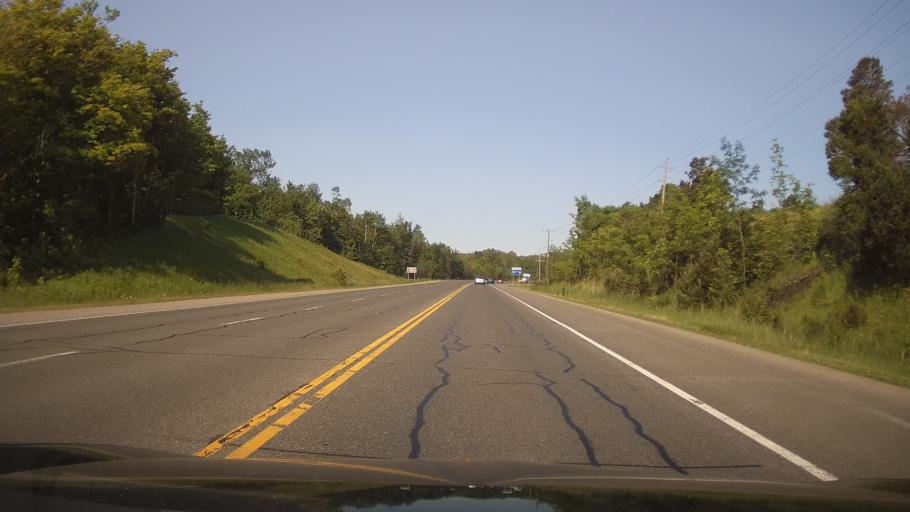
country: CA
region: Ontario
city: Peterborough
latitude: 44.3169
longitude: -78.1858
